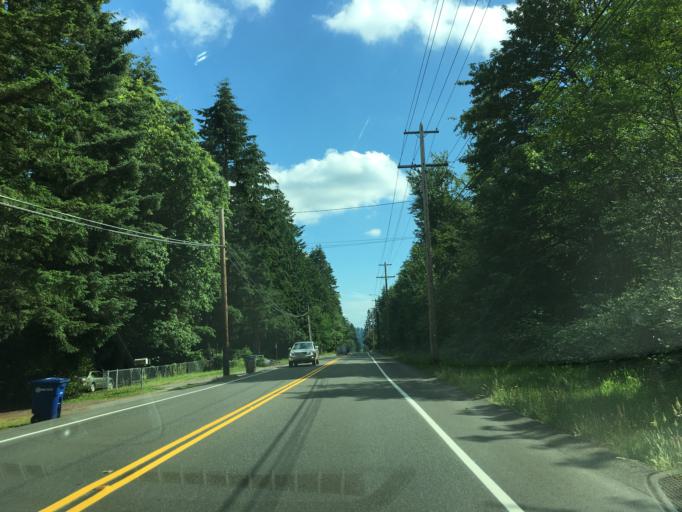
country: US
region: Washington
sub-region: King County
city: Kenmore
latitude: 47.7895
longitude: -122.2331
